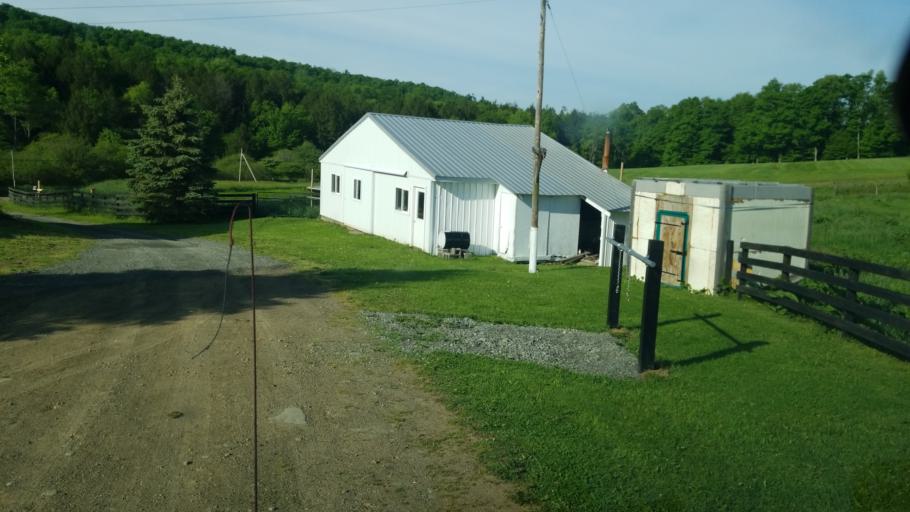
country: US
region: New York
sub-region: Allegany County
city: Andover
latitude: 41.9529
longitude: -77.7549
